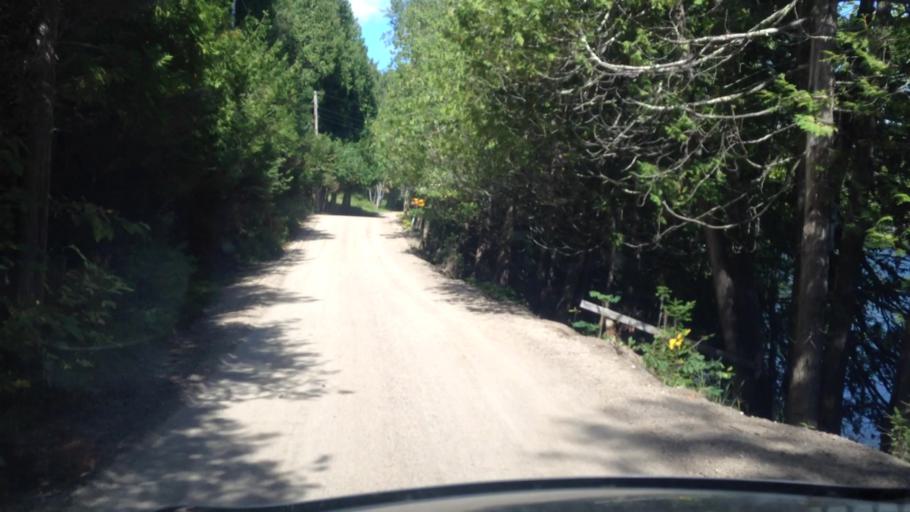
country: CA
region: Quebec
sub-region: Laurentides
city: Mont-Tremblant
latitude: 45.9380
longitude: -74.5847
